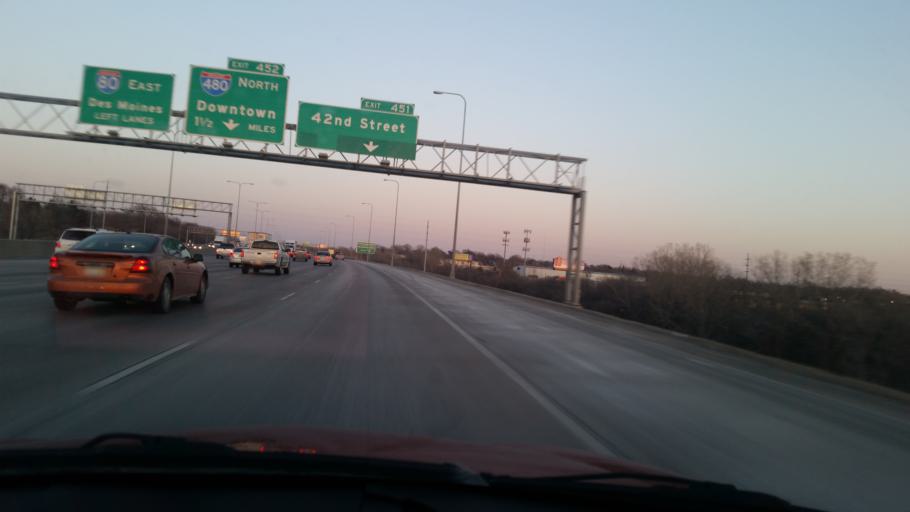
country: US
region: Nebraska
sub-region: Douglas County
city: Ralston
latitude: 41.2225
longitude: -95.9938
